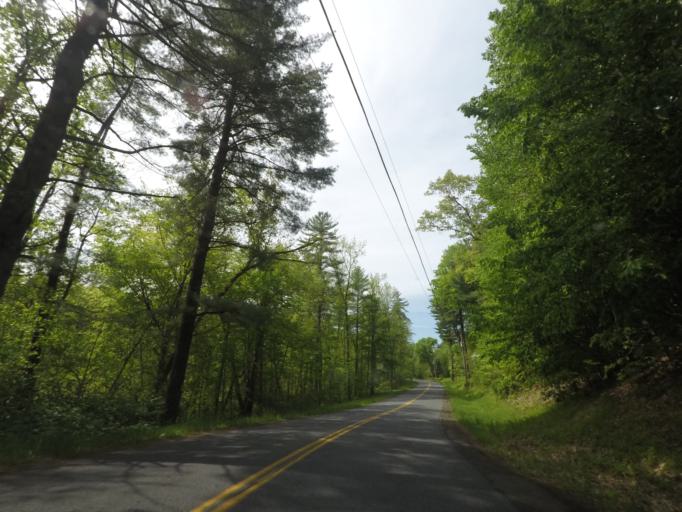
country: US
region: New York
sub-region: Saratoga County
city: Stillwater
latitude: 42.9852
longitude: -73.7145
